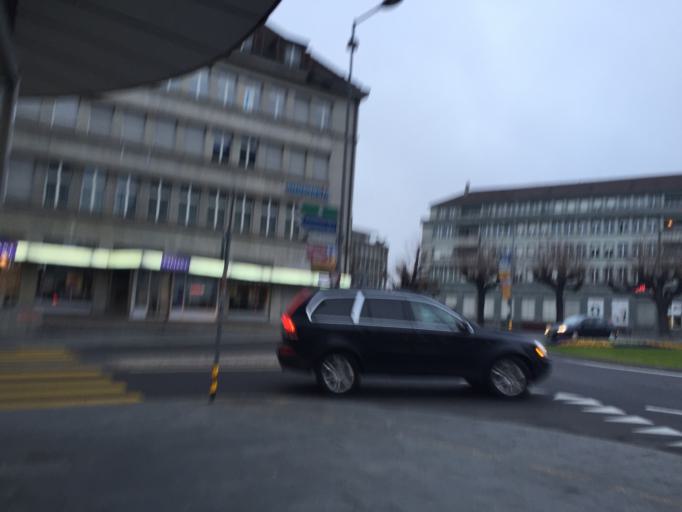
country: CH
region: Bern
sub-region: Thun District
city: Thun
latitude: 46.7560
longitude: 7.6301
